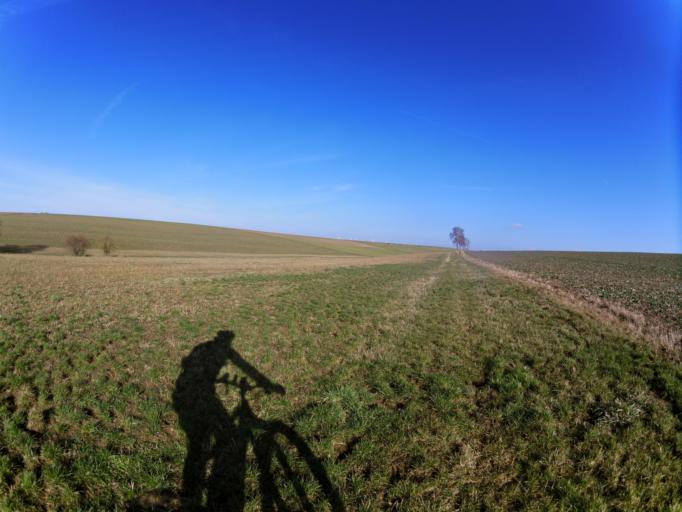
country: DE
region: Bavaria
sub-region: Regierungsbezirk Unterfranken
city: Giebelstadt
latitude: 49.6785
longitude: 9.9758
